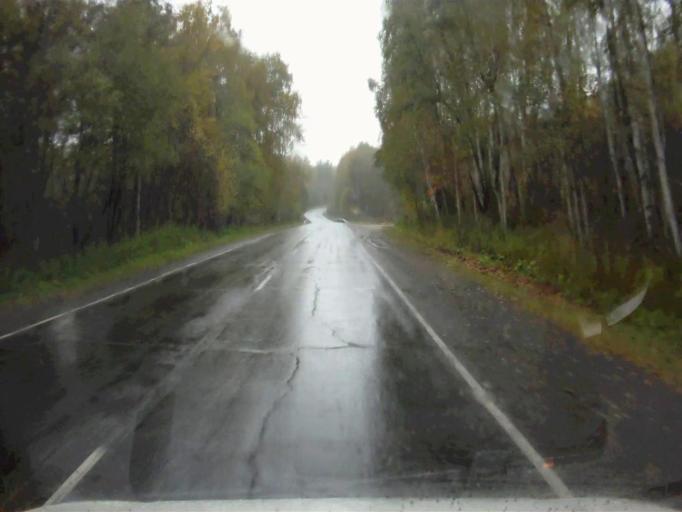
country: RU
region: Chelyabinsk
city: Kyshtym
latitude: 55.9097
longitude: 60.4360
